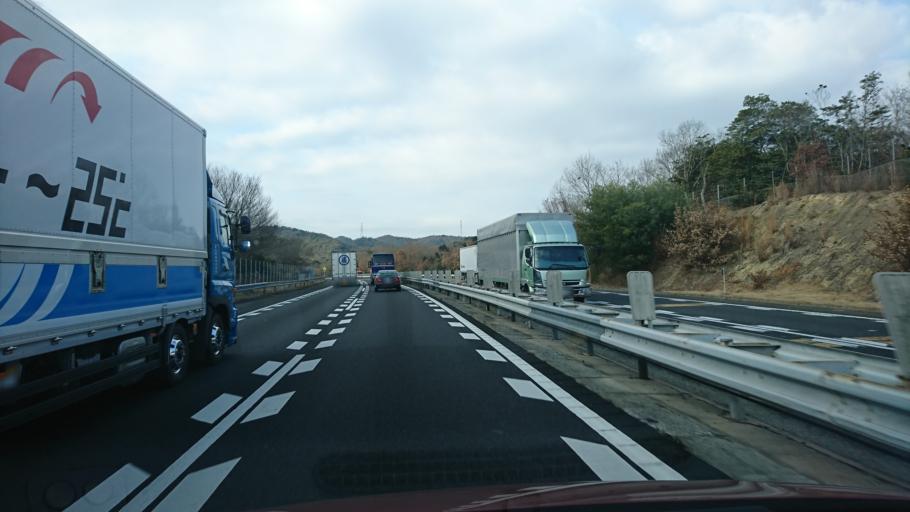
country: JP
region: Hyogo
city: Aioi
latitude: 34.8058
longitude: 134.4424
